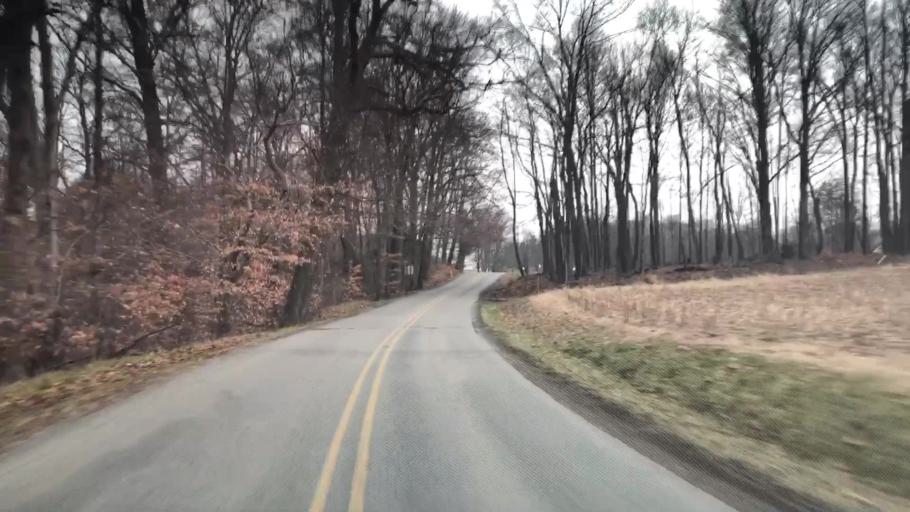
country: US
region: Pennsylvania
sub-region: Mercer County
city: Grove City
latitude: 41.1318
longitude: -80.0879
